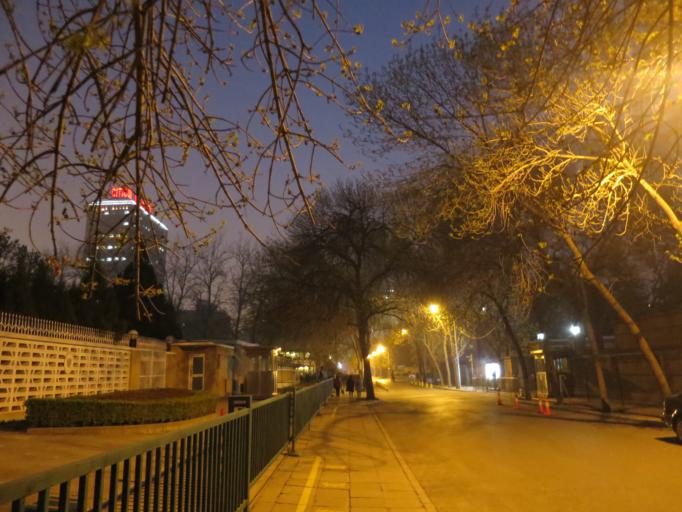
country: CN
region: Beijing
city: Chaowai
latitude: 39.9090
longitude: 116.4386
